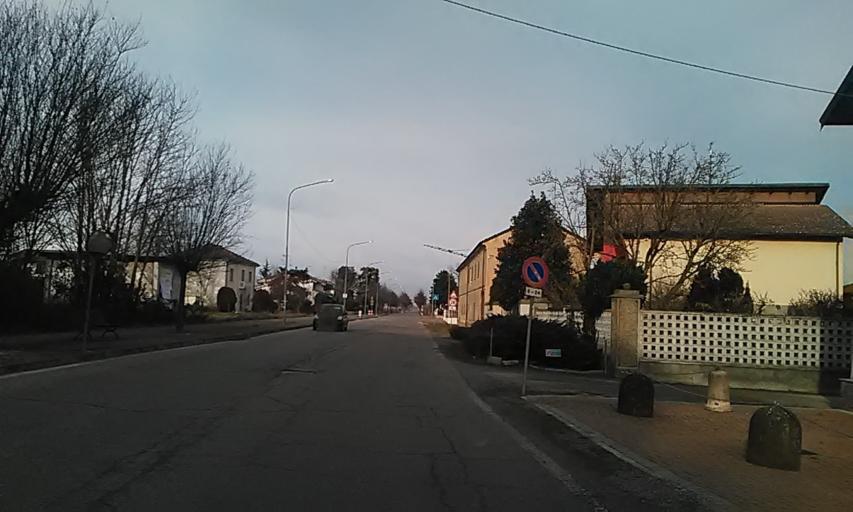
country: IT
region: Piedmont
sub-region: Provincia di Vercelli
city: Stroppiana
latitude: 45.2340
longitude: 8.4557
